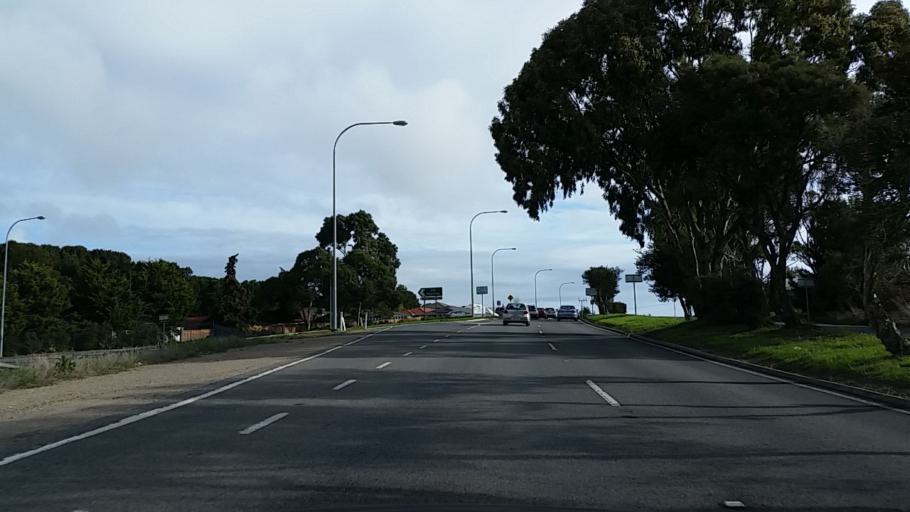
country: AU
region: South Australia
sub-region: Onkaparinga
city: Reynella
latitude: -35.0962
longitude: 138.5360
